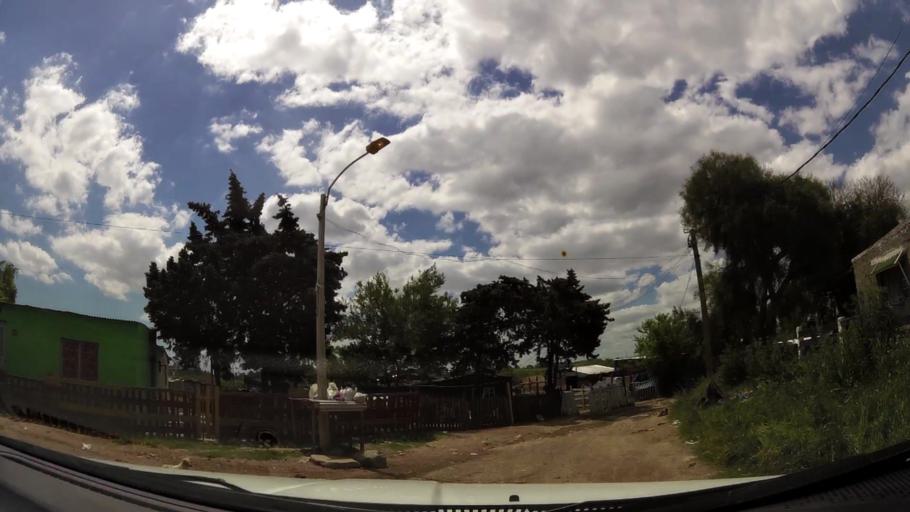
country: UY
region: Canelones
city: La Paz
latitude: -34.8185
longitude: -56.2480
